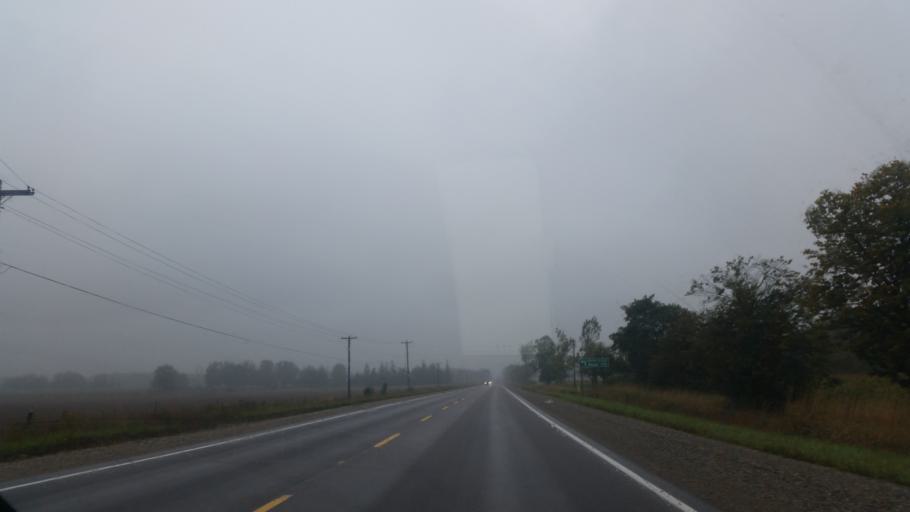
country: CA
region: Ontario
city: Stratford
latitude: 43.3009
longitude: -81.0419
